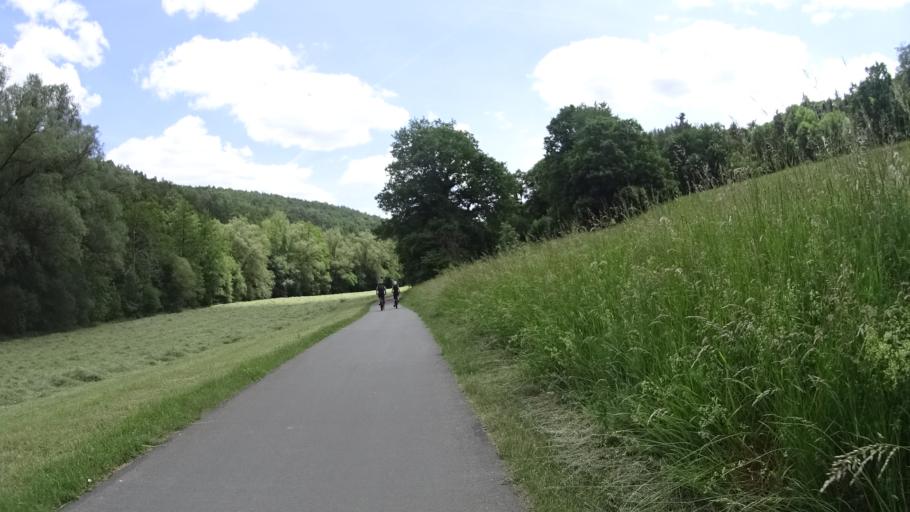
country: DE
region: Bavaria
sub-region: Regierungsbezirk Unterfranken
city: Eichenbuhl
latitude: 49.6887
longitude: 9.3512
